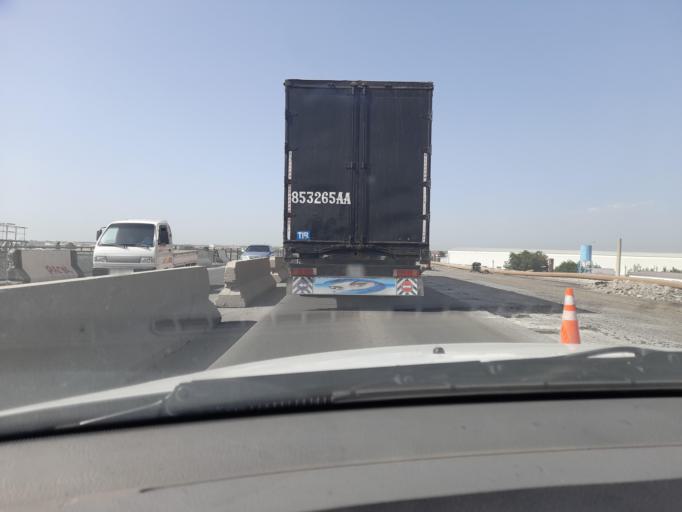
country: UZ
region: Samarqand
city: Samarqand
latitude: 39.6967
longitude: 67.0186
